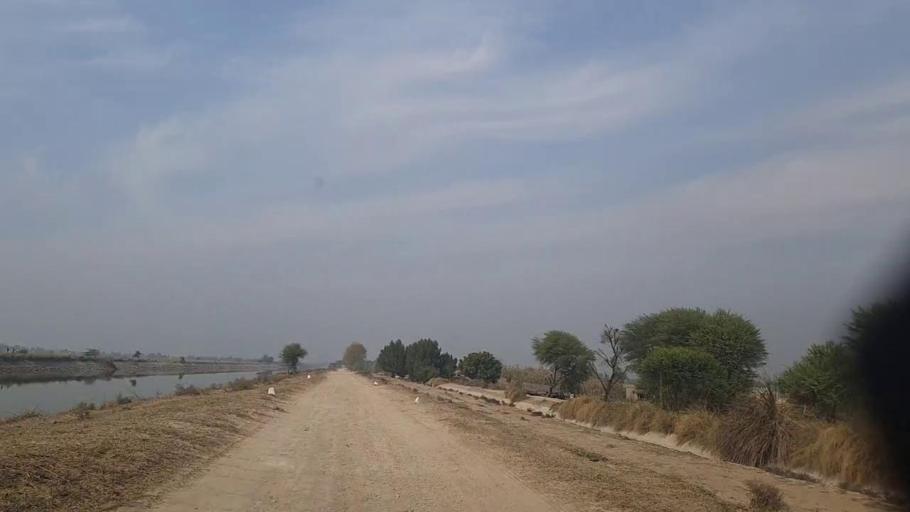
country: PK
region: Sindh
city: Daur
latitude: 26.3284
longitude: 68.1921
